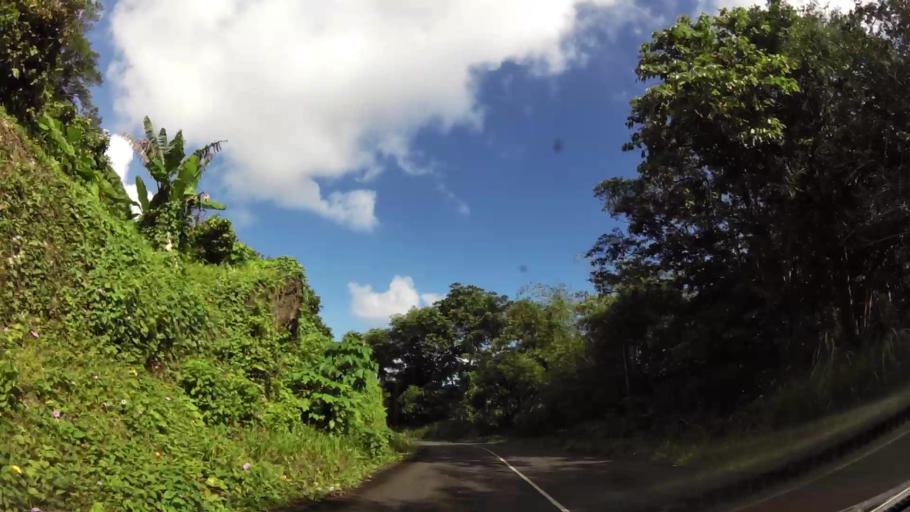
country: DM
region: Saint Andrew
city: Marigot
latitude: 15.5131
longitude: -61.2775
